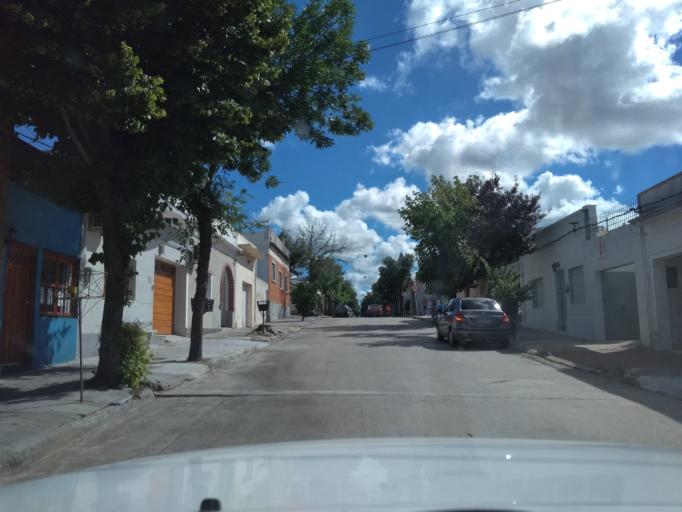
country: UY
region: Florida
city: Florida
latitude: -34.0986
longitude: -56.2114
